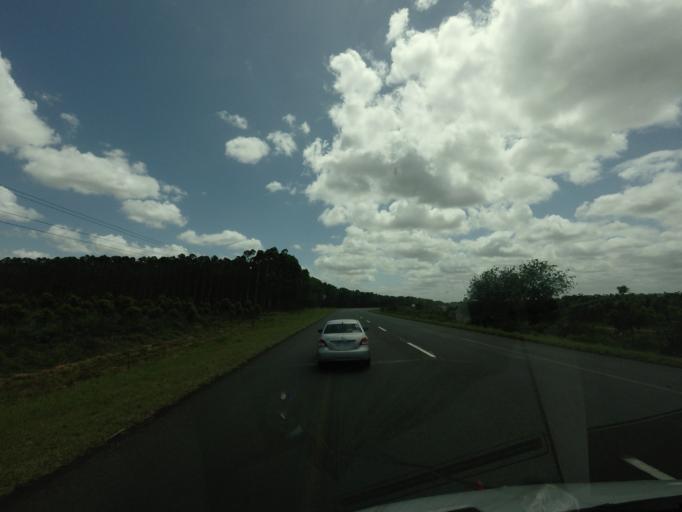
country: ZA
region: KwaZulu-Natal
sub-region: uThungulu District Municipality
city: KwaMbonambi
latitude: -28.5510
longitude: 32.1191
